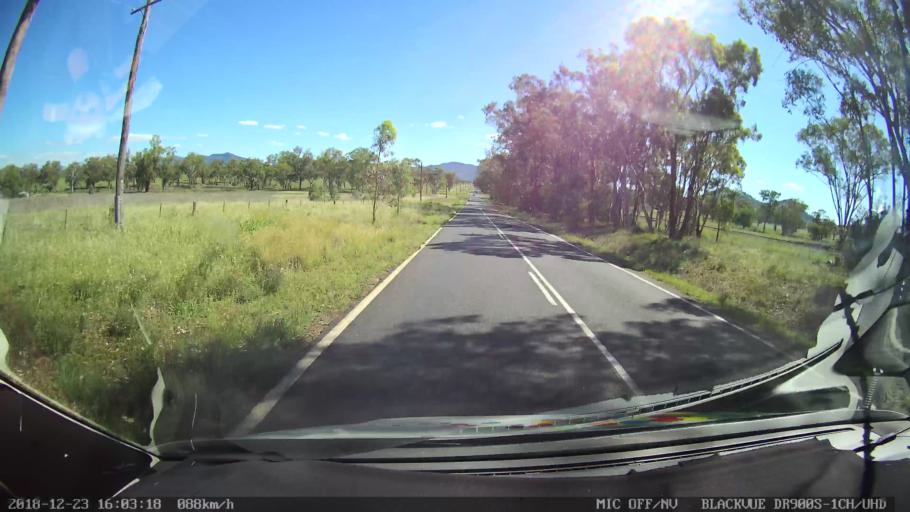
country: AU
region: New South Wales
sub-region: Tamworth Municipality
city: Phillip
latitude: -31.2419
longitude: 150.8019
